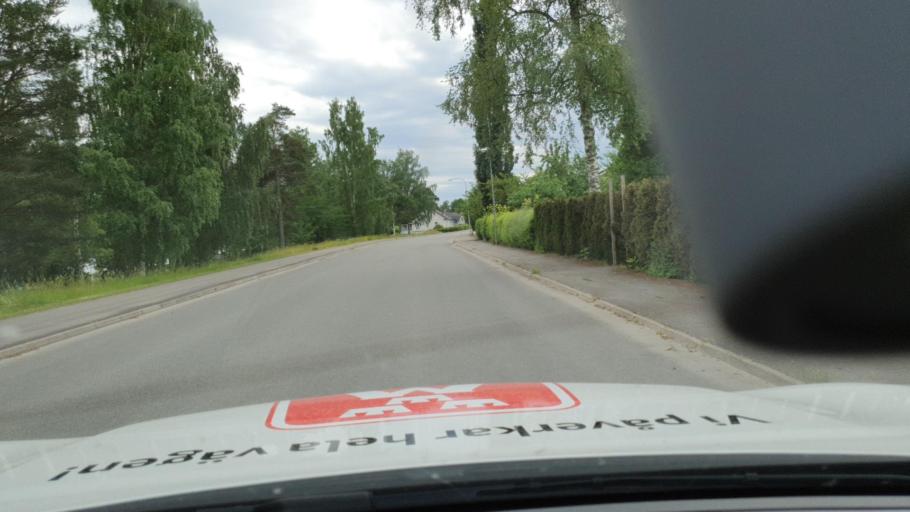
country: SE
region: Vaestra Goetaland
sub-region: Karlsborgs Kommun
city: Karlsborg
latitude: 58.5436
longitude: 14.4918
